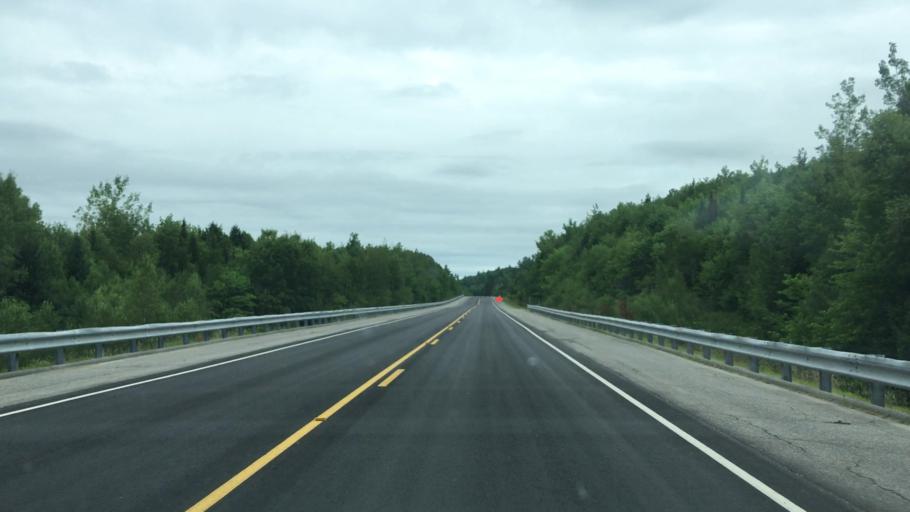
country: US
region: Maine
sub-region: Washington County
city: Cherryfield
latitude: 44.8894
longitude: -67.8565
